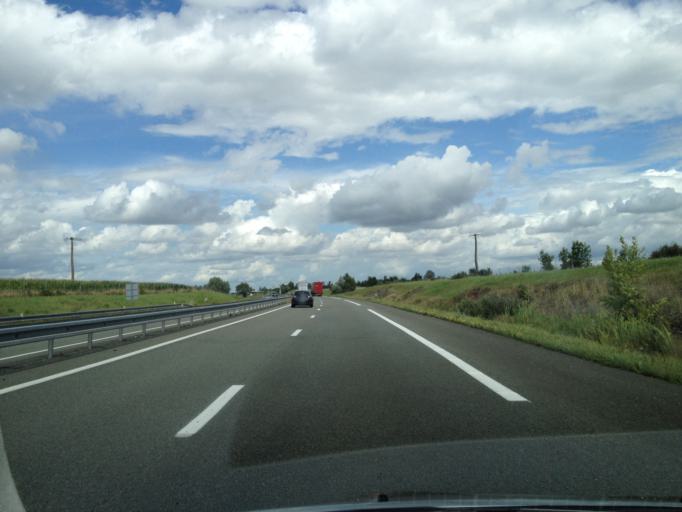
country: FR
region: Pays de la Loire
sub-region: Departement de la Sarthe
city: Montbizot
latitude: 48.1864
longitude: 0.1696
